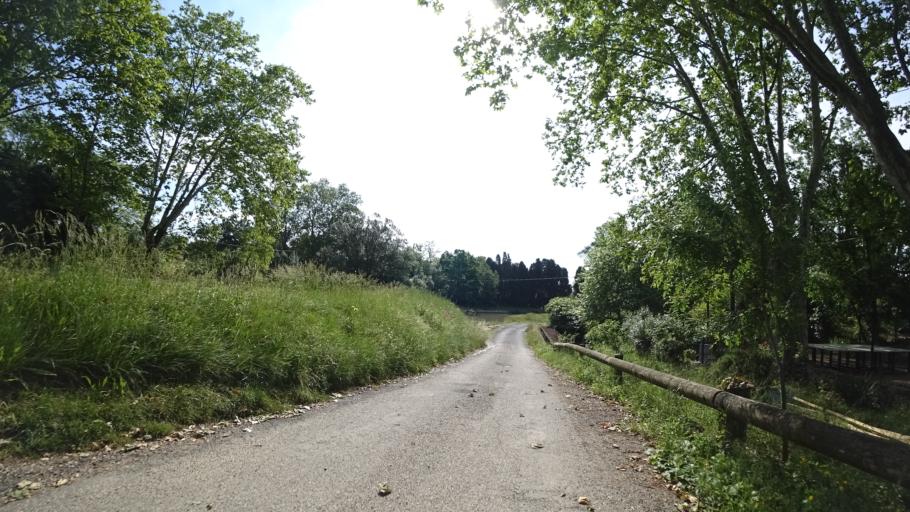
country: FR
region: Languedoc-Roussillon
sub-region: Departement de l'Herault
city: Olonzac
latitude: 43.2693
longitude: 2.7387
